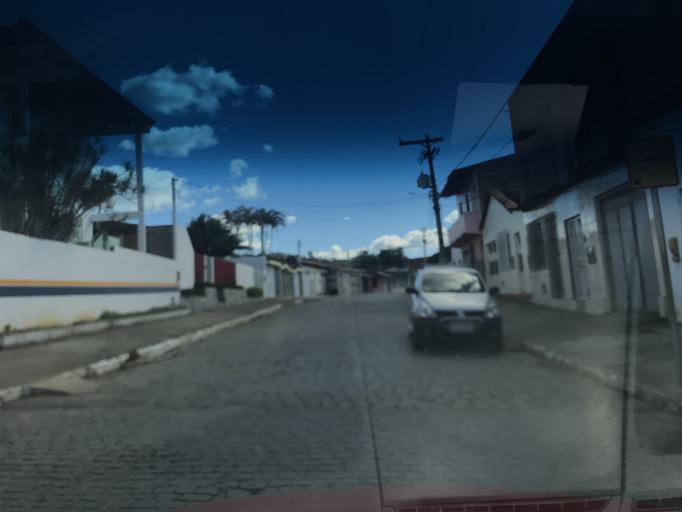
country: BR
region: Bahia
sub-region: Gandu
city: Gandu
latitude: -13.7462
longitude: -39.4906
